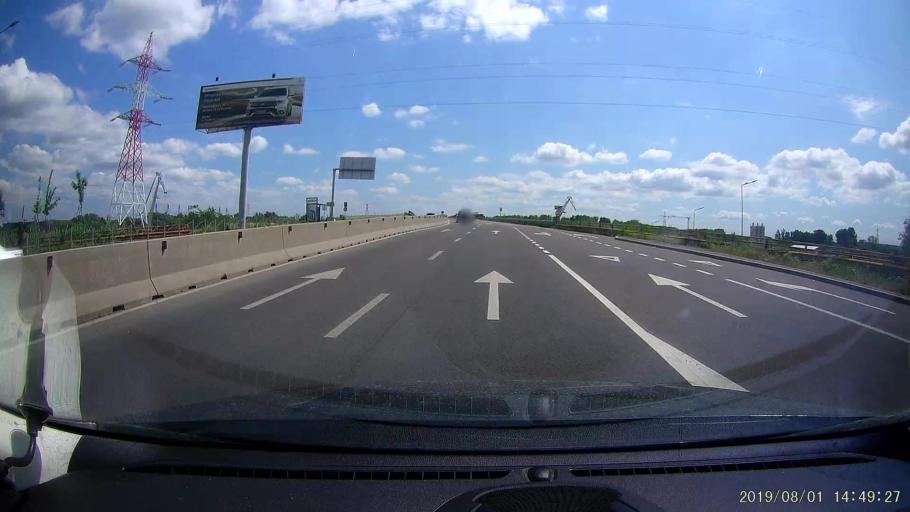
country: RO
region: Galati
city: Galati
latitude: 45.4043
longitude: 28.0151
